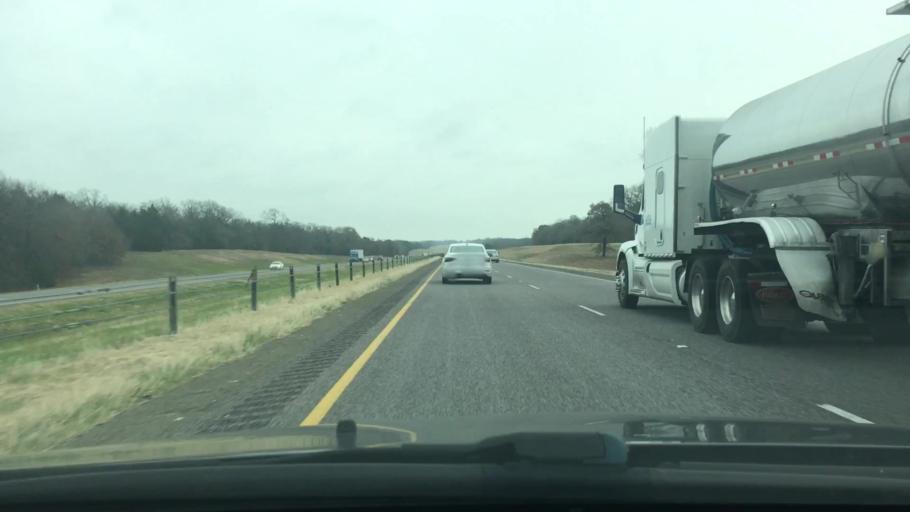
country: US
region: Texas
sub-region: Freestone County
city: Fairfield
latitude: 31.7577
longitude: -96.2069
